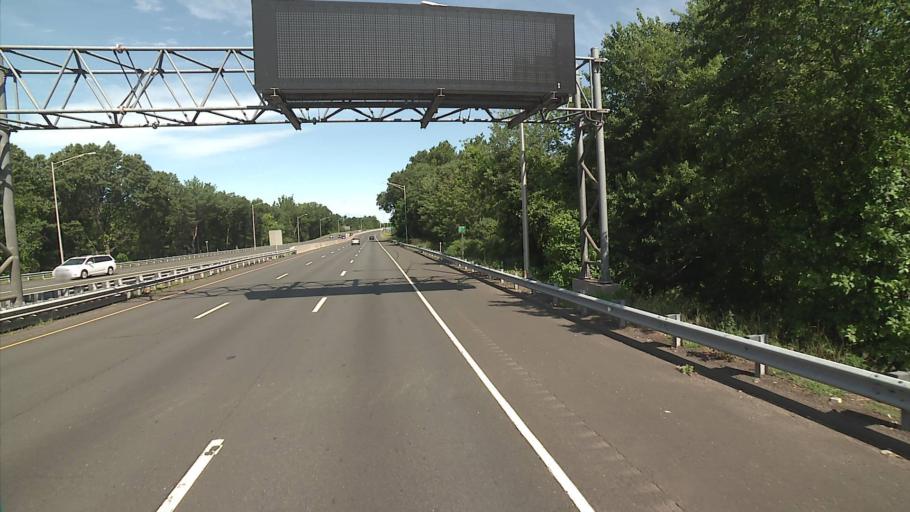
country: US
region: Connecticut
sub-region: Hartford County
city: Glastonbury
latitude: 41.7187
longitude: -72.6021
